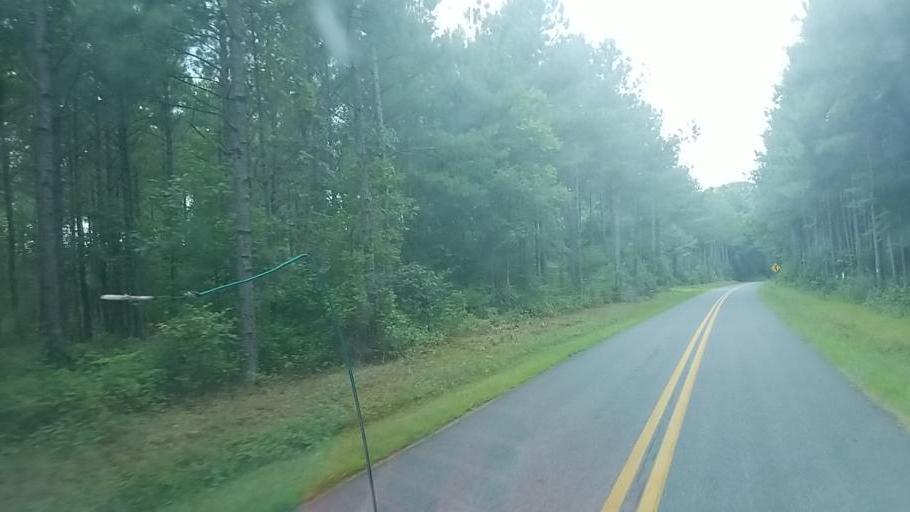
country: US
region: Maryland
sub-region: Worcester County
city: Snow Hill
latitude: 38.2616
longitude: -75.4548
